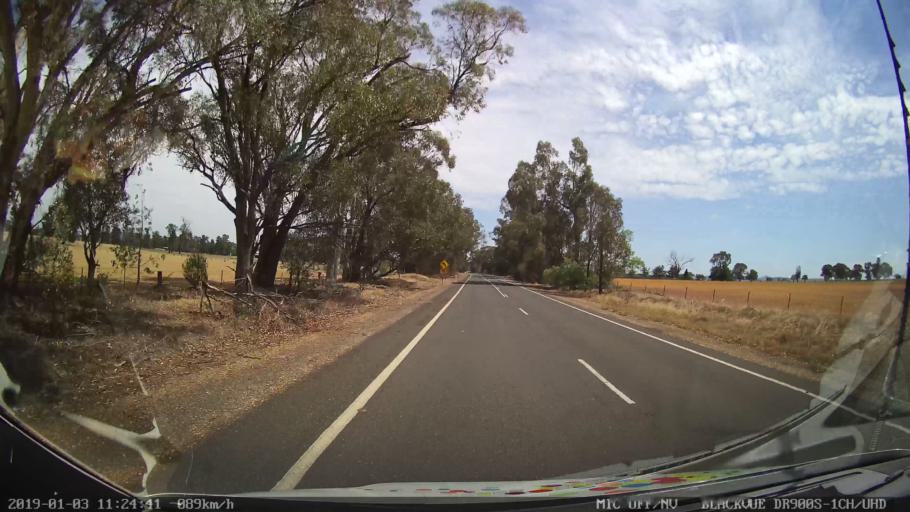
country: AU
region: New South Wales
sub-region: Weddin
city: Grenfell
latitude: -34.0483
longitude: 148.2334
